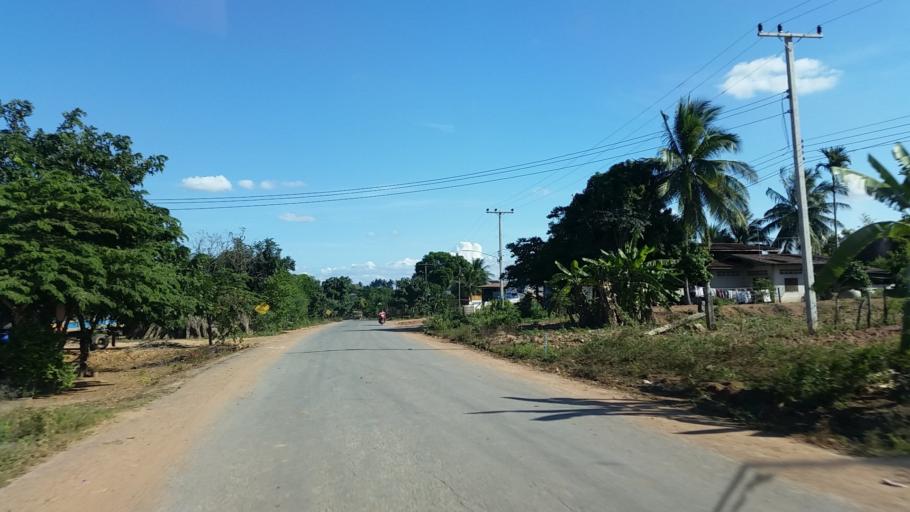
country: TH
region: Chaiyaphum
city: Thep Sathit
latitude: 15.5438
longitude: 101.4816
